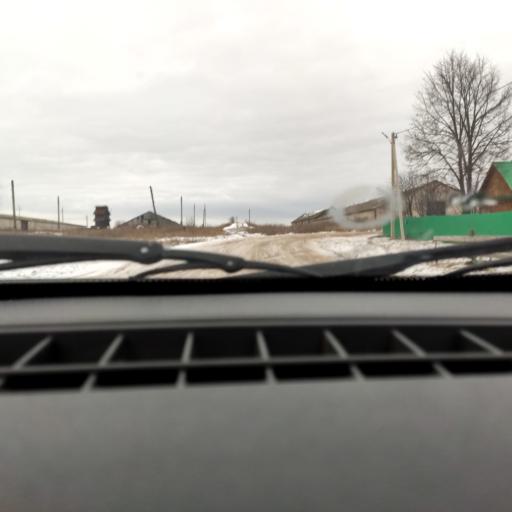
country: RU
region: Bashkortostan
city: Tolbazy
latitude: 54.2578
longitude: 55.9270
